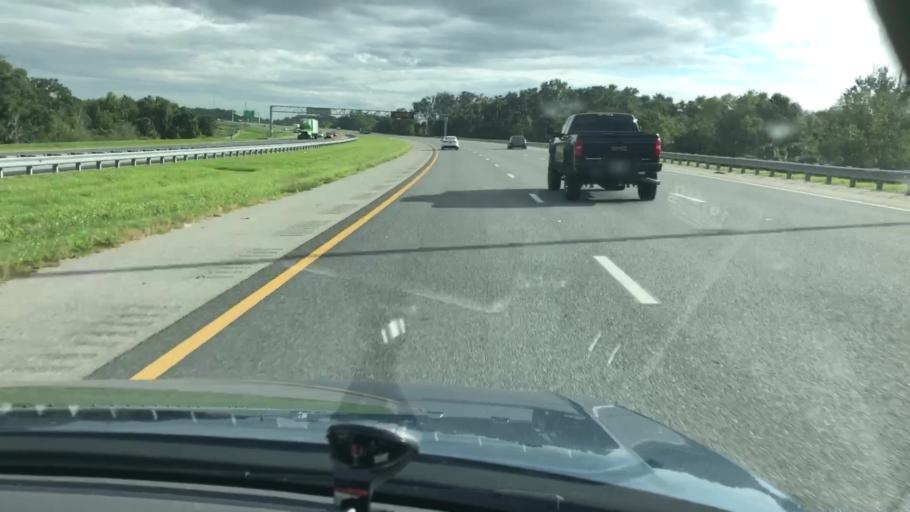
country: US
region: Florida
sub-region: Orange County
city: Apopka
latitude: 28.6778
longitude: -81.5597
